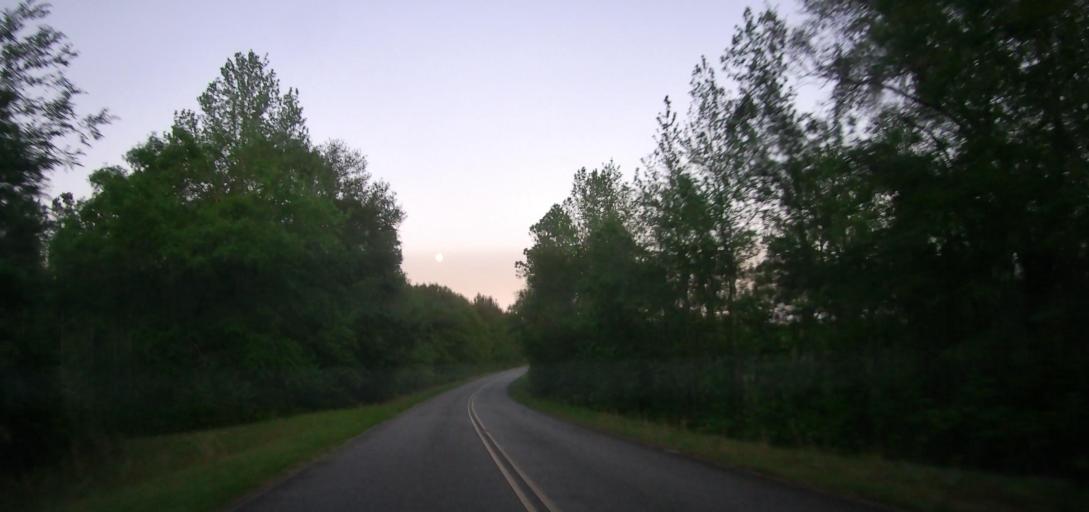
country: US
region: Georgia
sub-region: Marion County
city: Buena Vista
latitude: 32.2570
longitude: -84.5924
